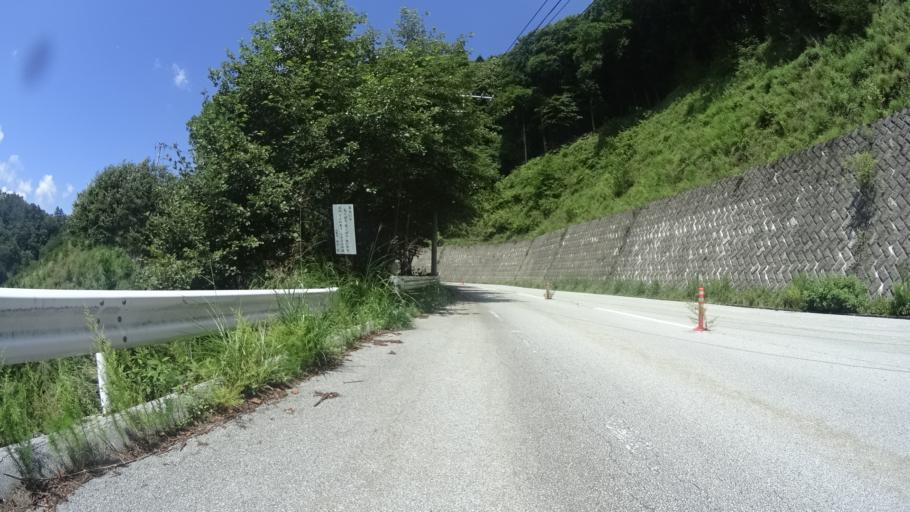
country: JP
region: Yamanashi
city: Enzan
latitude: 35.8054
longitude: 138.6649
